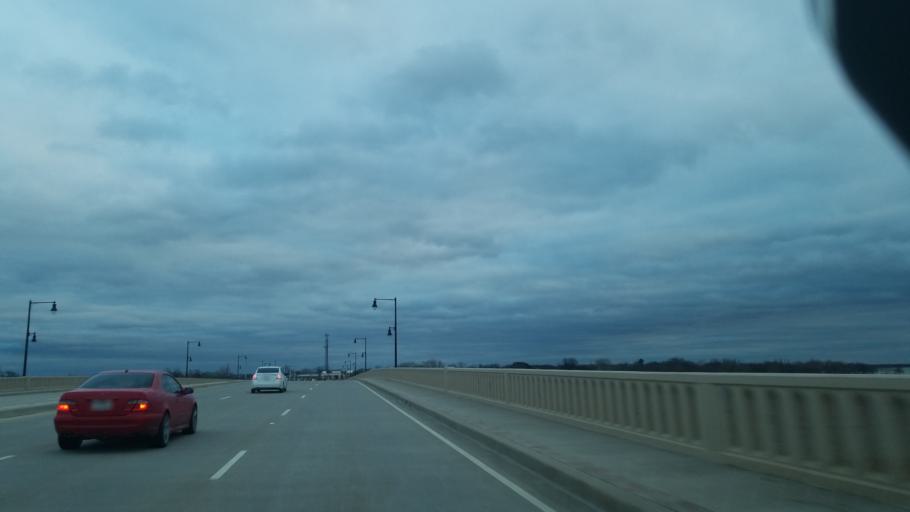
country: US
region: Texas
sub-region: Denton County
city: Little Elm
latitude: 33.1589
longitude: -96.9543
